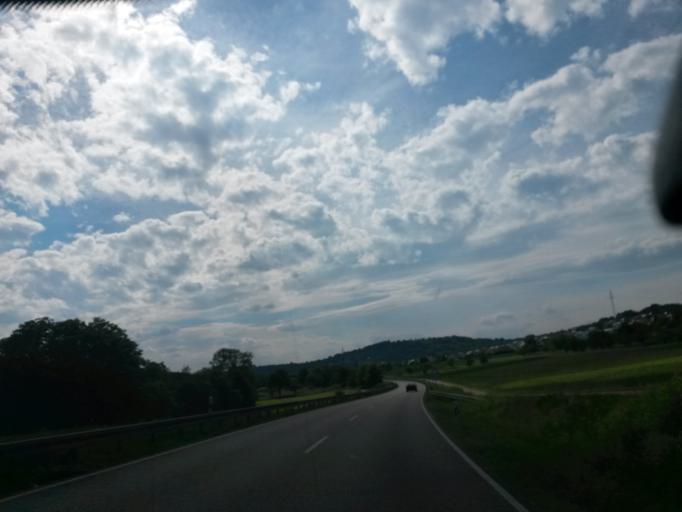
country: DE
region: Baden-Wuerttemberg
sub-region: Karlsruhe Region
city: Simmozheim
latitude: 48.7489
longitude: 8.8297
